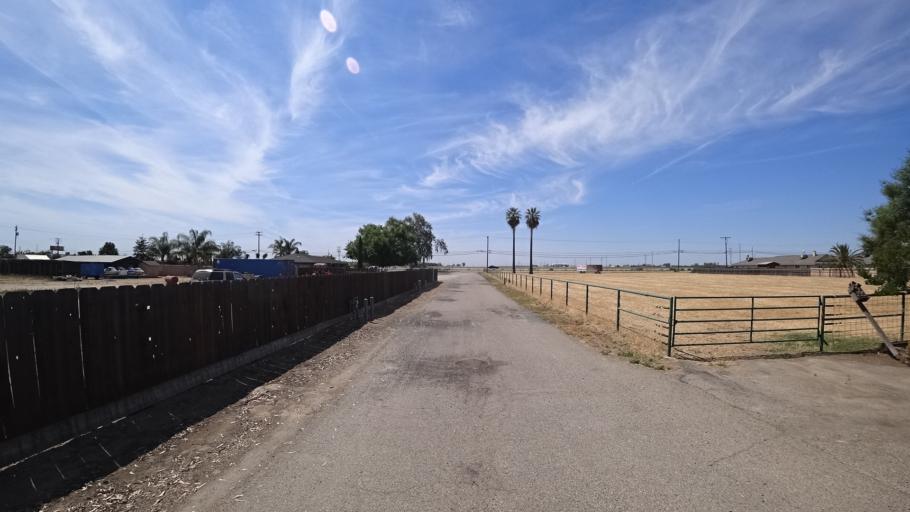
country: US
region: California
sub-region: Kings County
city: Home Garden
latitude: 36.3292
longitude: -119.5884
